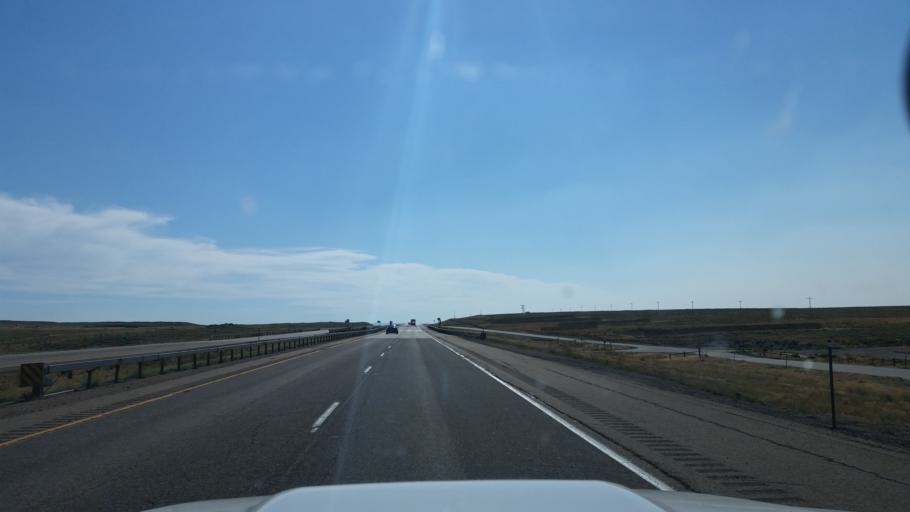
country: US
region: Wyoming
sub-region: Uinta County
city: Lyman
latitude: 41.4340
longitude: -110.1066
